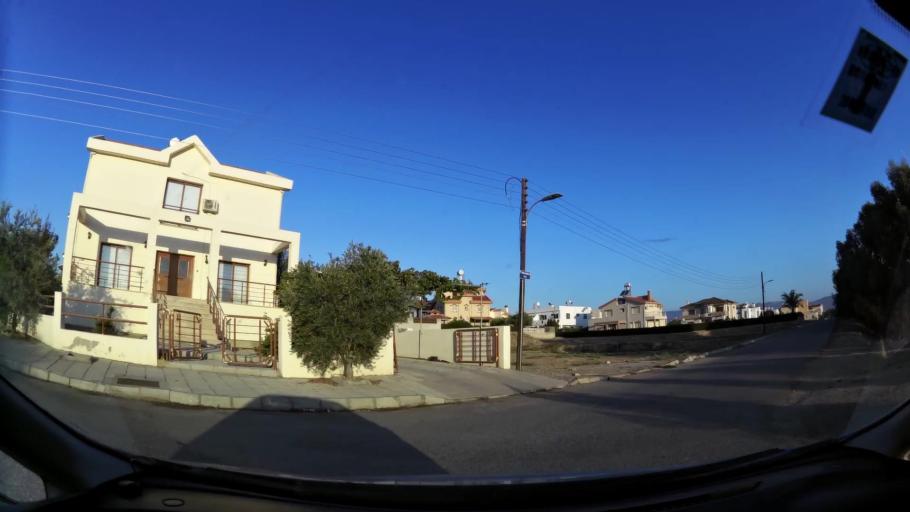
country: CY
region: Lefkosia
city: Nicosia
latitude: 35.1907
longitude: 33.3187
